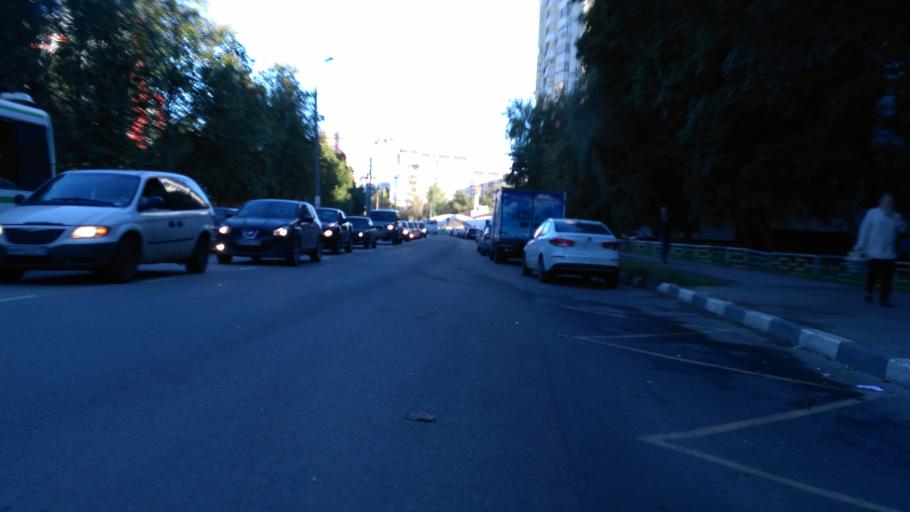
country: RU
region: Moscow
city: Likhobory
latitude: 55.8599
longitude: 37.5627
